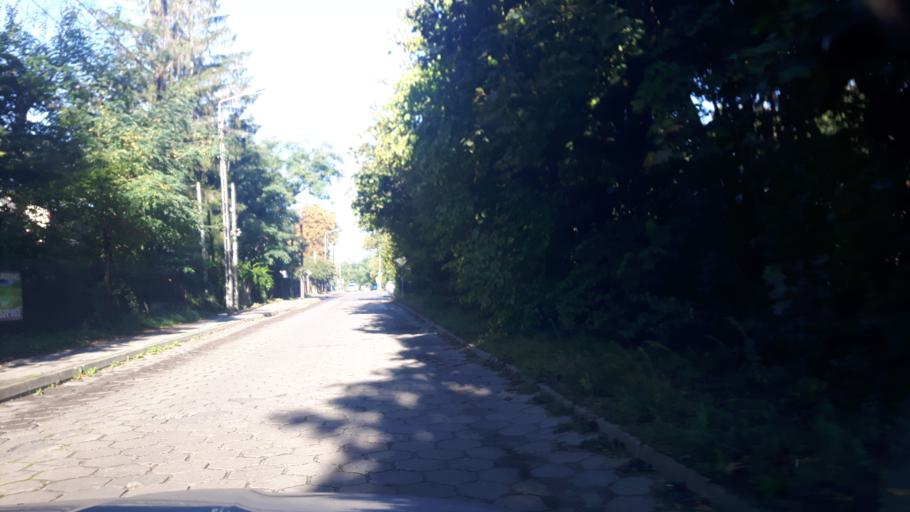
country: PL
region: Masovian Voivodeship
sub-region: Warszawa
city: Bialoleka
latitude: 52.3380
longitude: 20.9956
